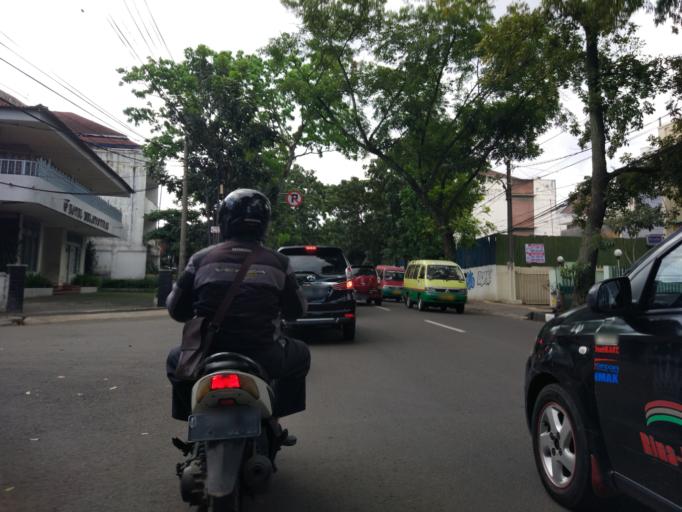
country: ID
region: West Java
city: Bandung
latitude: -6.9235
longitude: 107.6234
